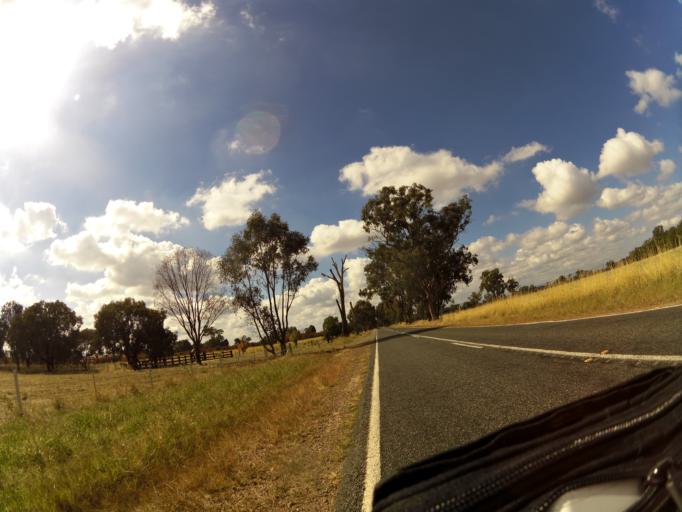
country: AU
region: Victoria
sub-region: Benalla
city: Benalla
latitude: -36.6059
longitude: 146.0134
